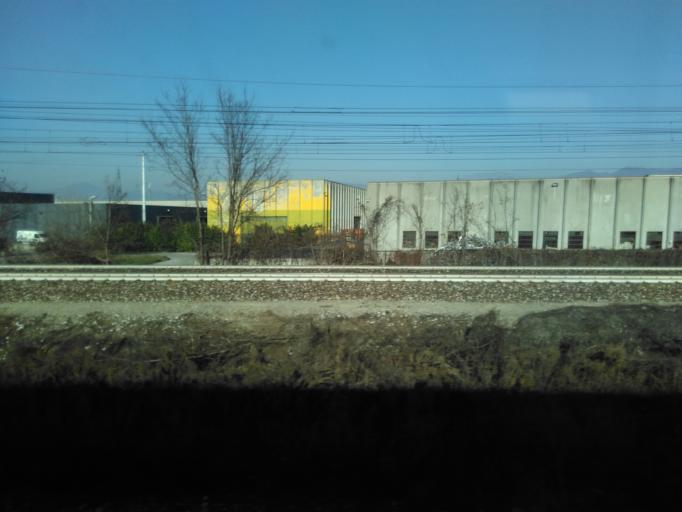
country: IT
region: Lombardy
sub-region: Provincia di Brescia
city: Castegnato
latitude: 45.5483
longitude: 10.1216
